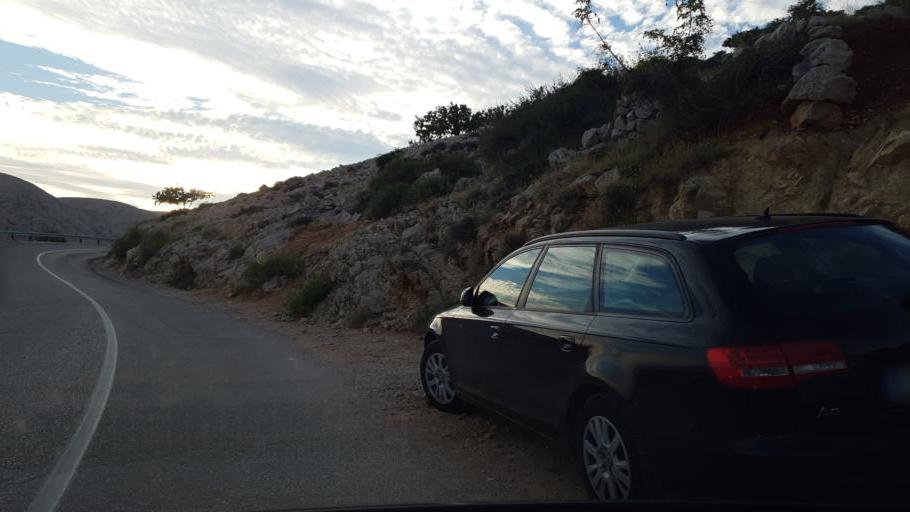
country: HR
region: Primorsko-Goranska
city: Punat
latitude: 44.9665
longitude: 14.6689
